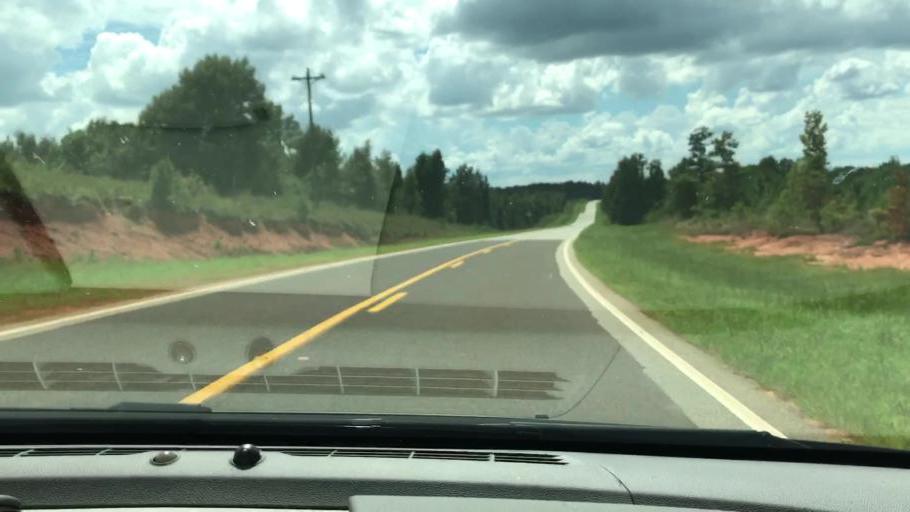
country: US
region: Georgia
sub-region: Quitman County
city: Georgetown
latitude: 31.9106
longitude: -85.0604
